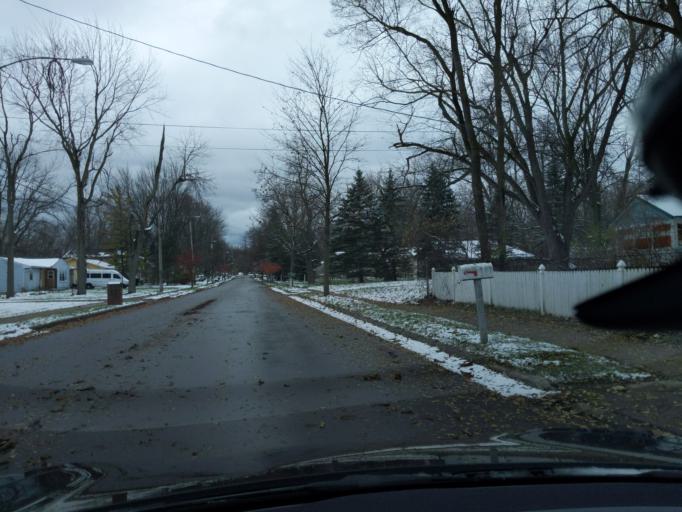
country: US
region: Michigan
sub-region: Ingham County
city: Lansing
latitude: 42.6861
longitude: -84.5886
